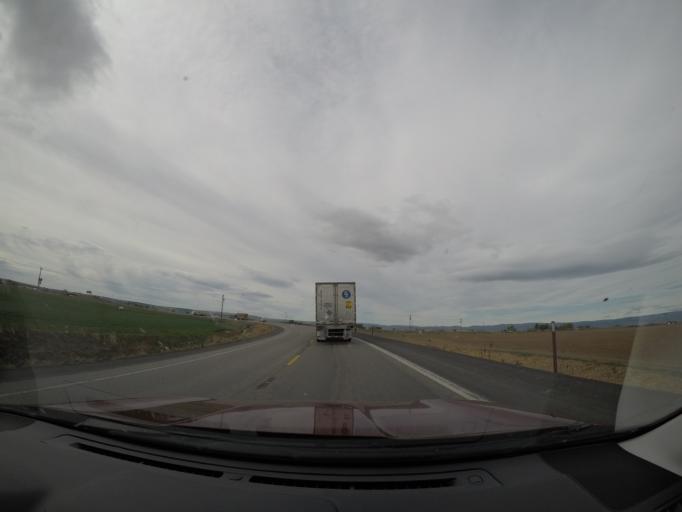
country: US
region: Washington
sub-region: Grant County
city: Quincy
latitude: 47.0898
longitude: -119.8626
